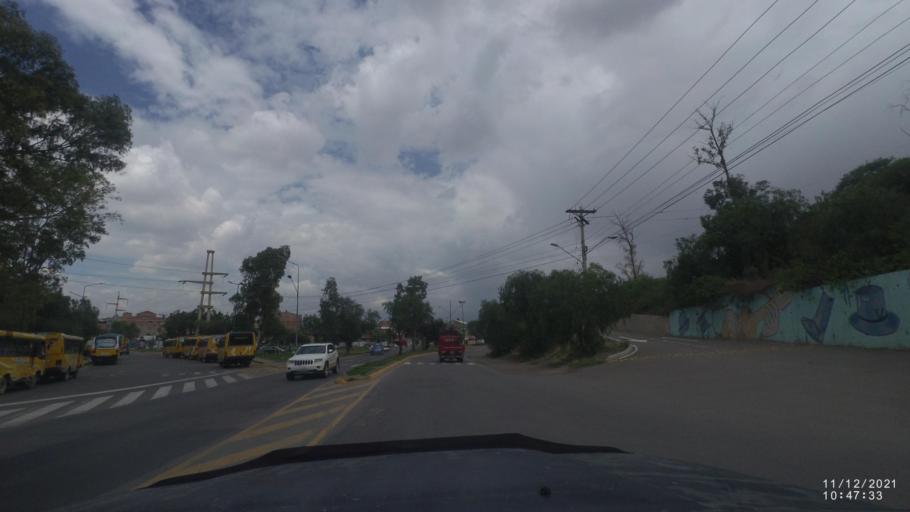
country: BO
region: Cochabamba
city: Cochabamba
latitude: -17.3993
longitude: -66.1347
